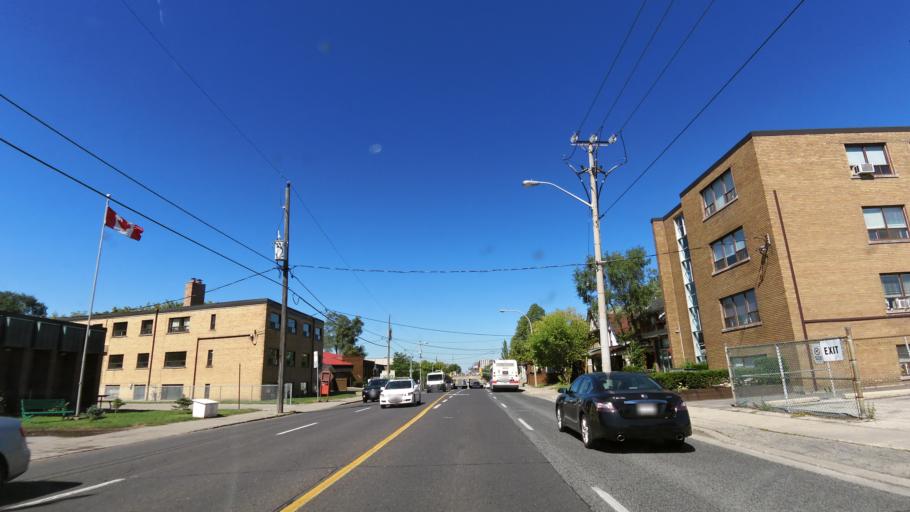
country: CA
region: Ontario
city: Etobicoke
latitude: 43.6642
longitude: -79.4906
